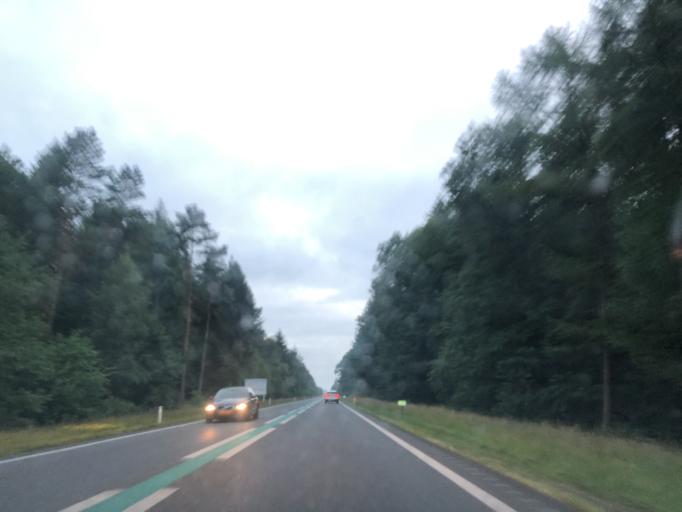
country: NL
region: Drenthe
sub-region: Gemeente Borger-Odoorn
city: Borger
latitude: 52.9576
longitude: 6.7814
